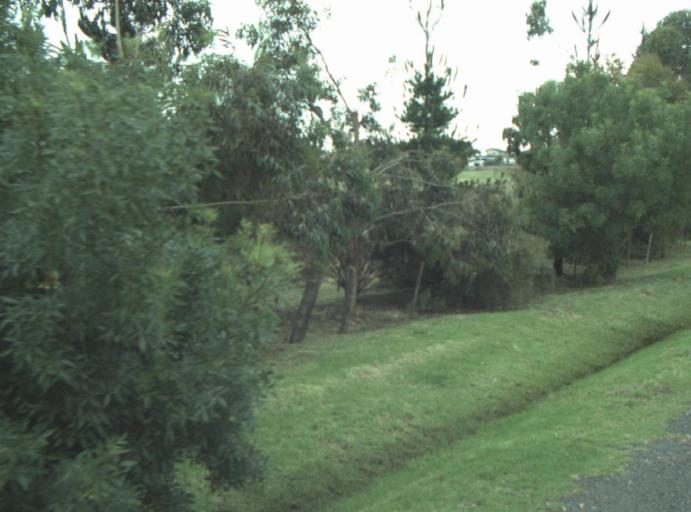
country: AU
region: Victoria
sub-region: Greater Geelong
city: Breakwater
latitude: -38.1901
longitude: 144.3878
